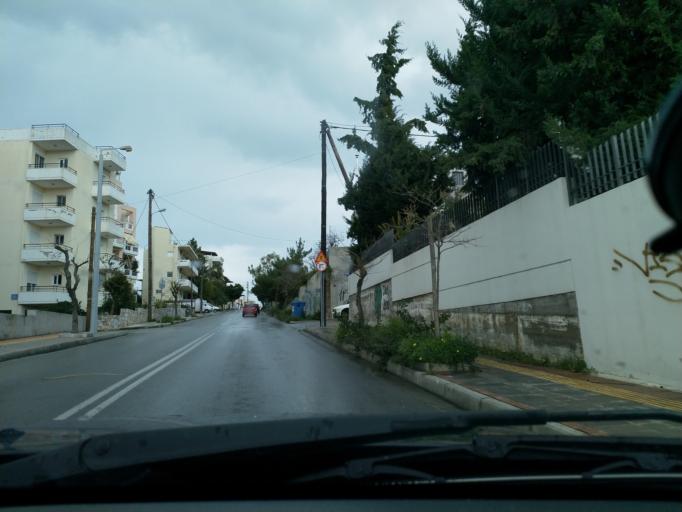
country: GR
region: Crete
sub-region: Nomos Chanias
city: Chania
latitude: 35.5128
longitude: 24.0444
